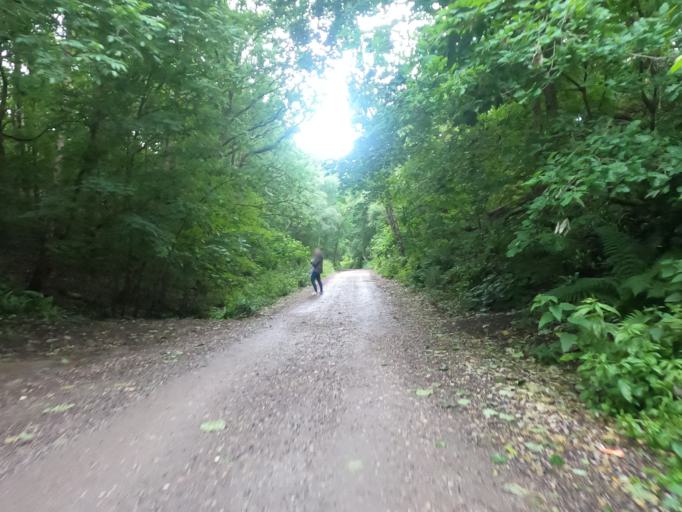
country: GB
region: England
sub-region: Cheshire West and Chester
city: Winsford
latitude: 53.2159
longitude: -2.5210
